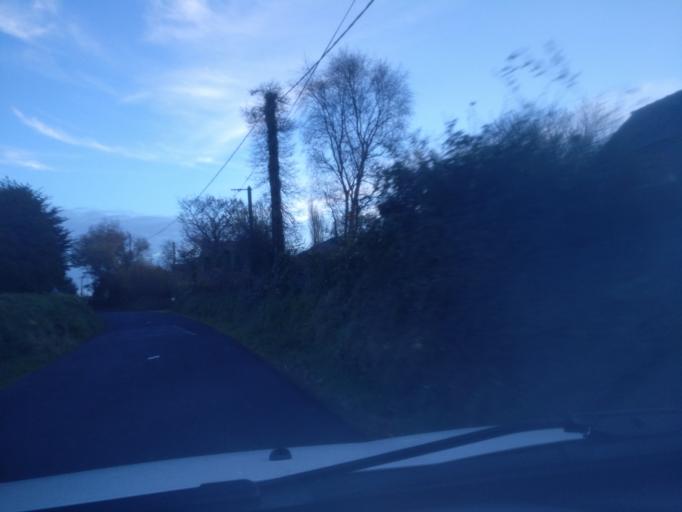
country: FR
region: Brittany
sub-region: Departement des Cotes-d'Armor
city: Saint-Quay-Perros
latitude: 48.8036
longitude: -3.4643
